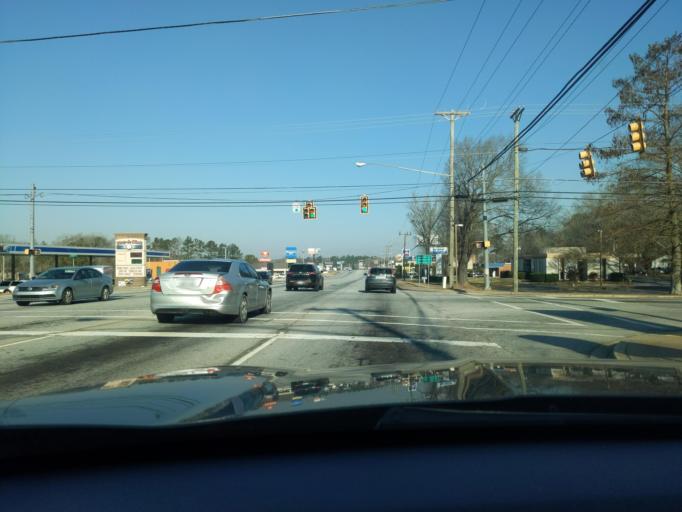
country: US
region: South Carolina
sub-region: Greenwood County
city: Greenwood
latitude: 34.2095
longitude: -82.1469
